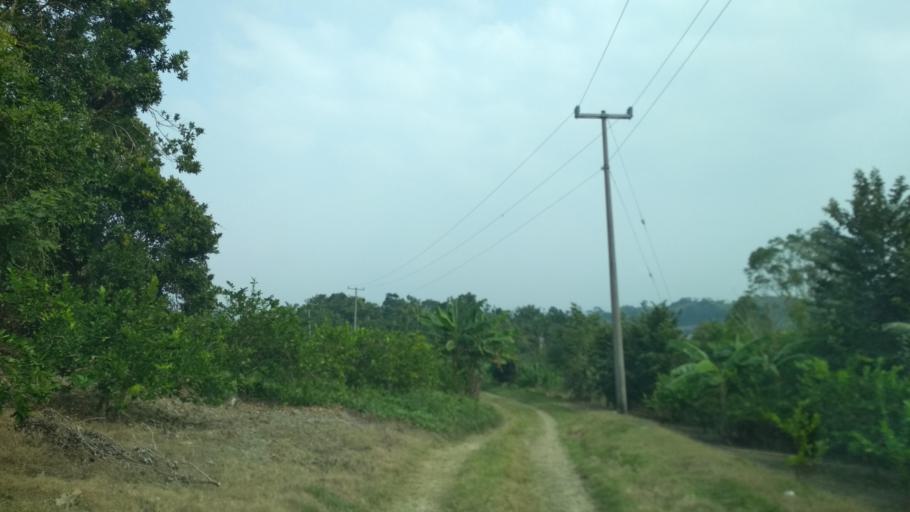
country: MM
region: Kayah
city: Loikaw
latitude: 20.2040
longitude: 97.3241
